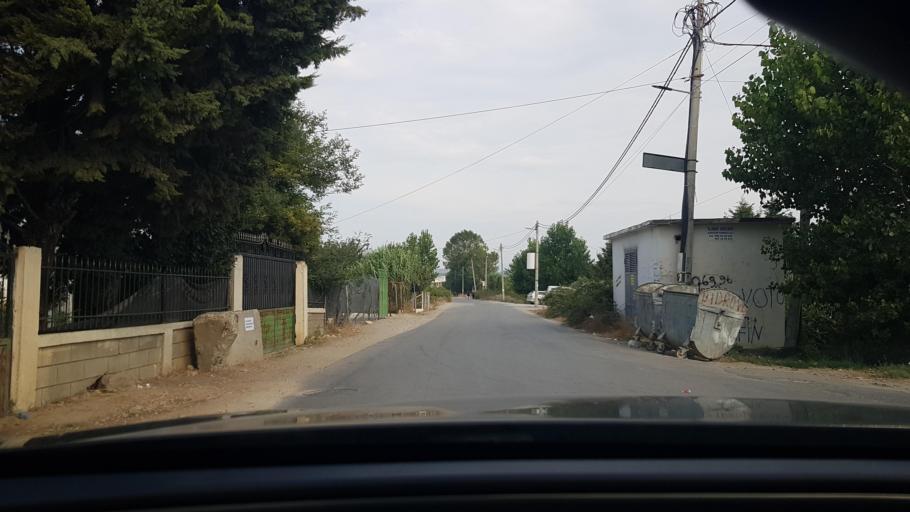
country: AL
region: Durres
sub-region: Rrethi i Durresit
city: Katundi i Ri
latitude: 41.4863
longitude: 19.5194
